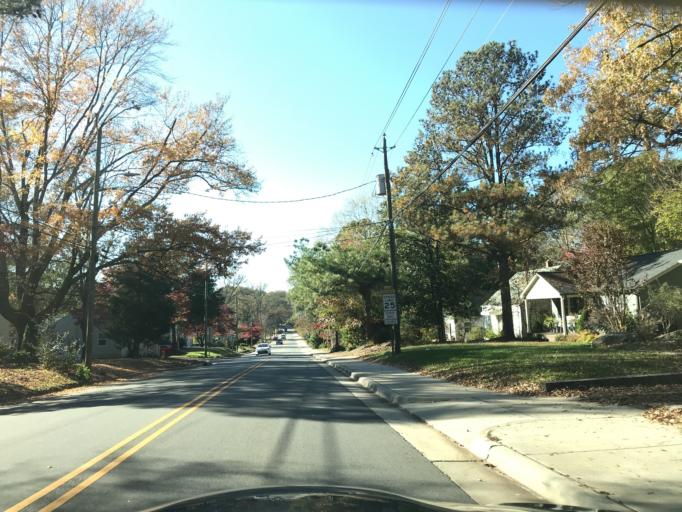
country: US
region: North Carolina
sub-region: Wake County
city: Raleigh
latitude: 35.7929
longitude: -78.6216
